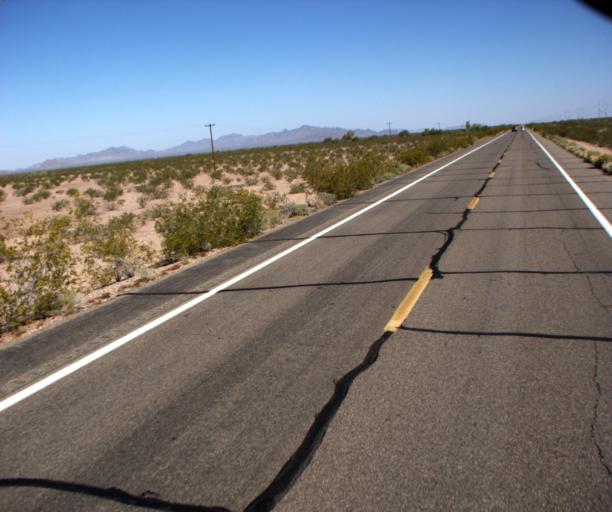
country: US
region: Arizona
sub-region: La Paz County
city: Quartzsite
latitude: 33.3456
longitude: -114.2170
